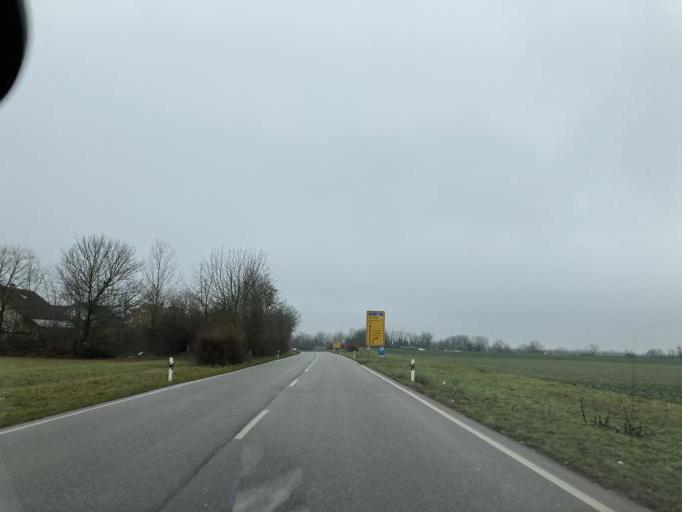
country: DE
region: Baden-Wuerttemberg
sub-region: Freiburg Region
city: Neuenburg am Rhein
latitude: 47.8191
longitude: 7.5748
